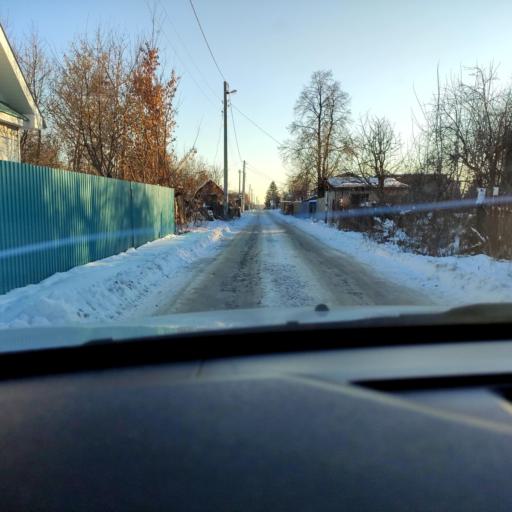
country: RU
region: Samara
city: Petra-Dubrava
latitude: 53.2871
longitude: 50.2911
